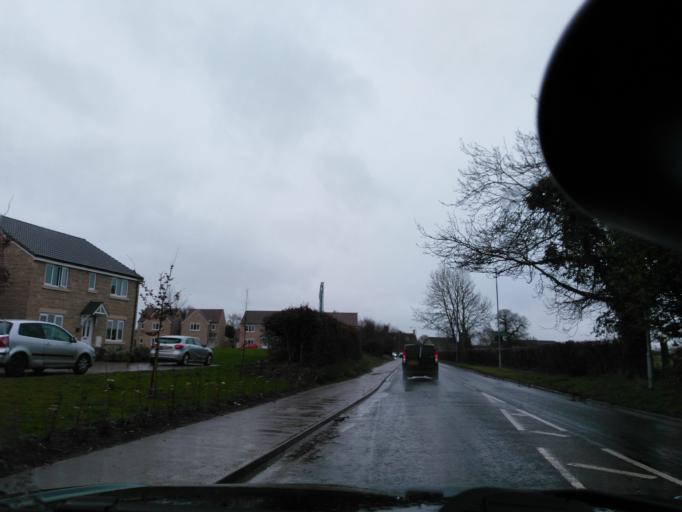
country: GB
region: England
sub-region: Wiltshire
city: Melksham
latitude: 51.3827
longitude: -2.1516
